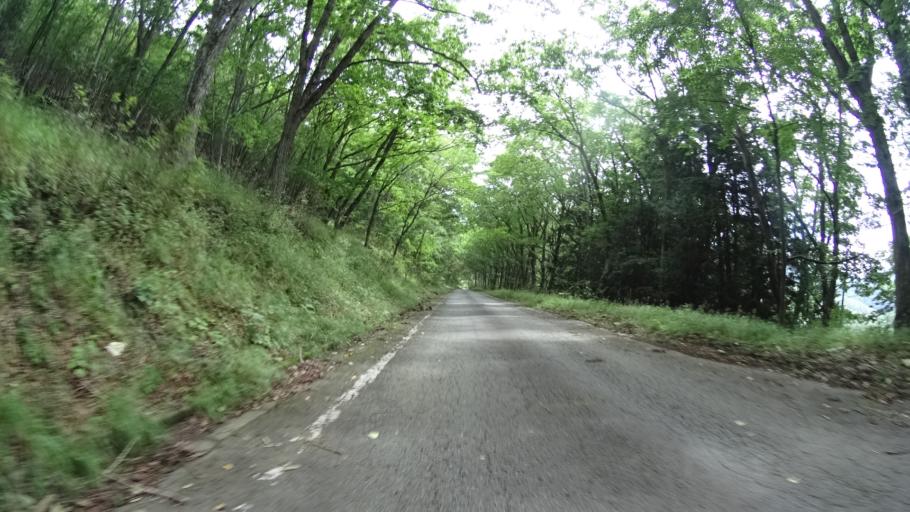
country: JP
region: Yamanashi
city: Kofu-shi
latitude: 35.8169
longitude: 138.5550
